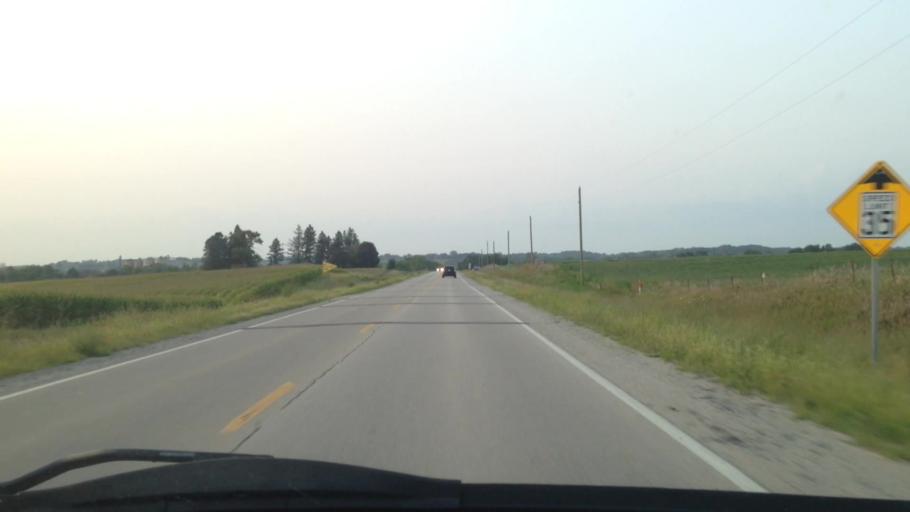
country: US
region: Iowa
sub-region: Linn County
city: Palo
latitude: 42.0823
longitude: -91.8689
